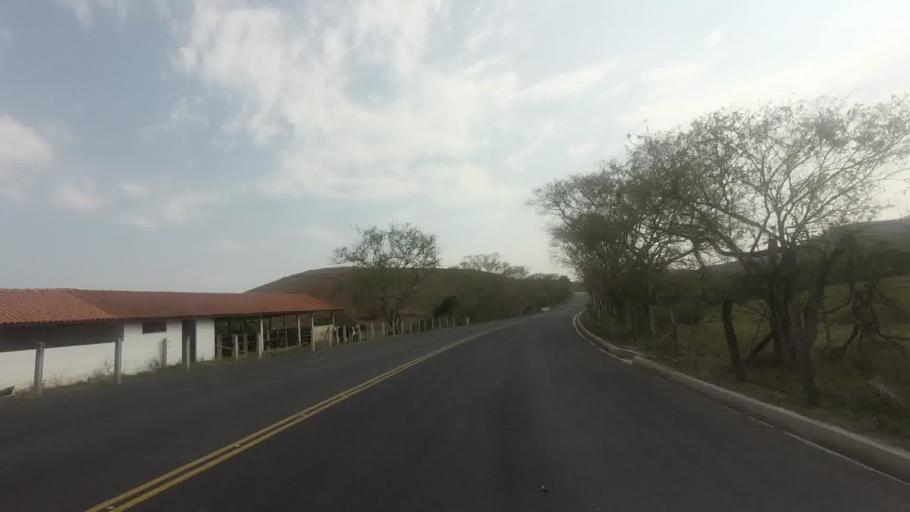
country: BR
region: Rio de Janeiro
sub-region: Itaperuna
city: Itaperuna
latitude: -21.2651
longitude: -41.7716
